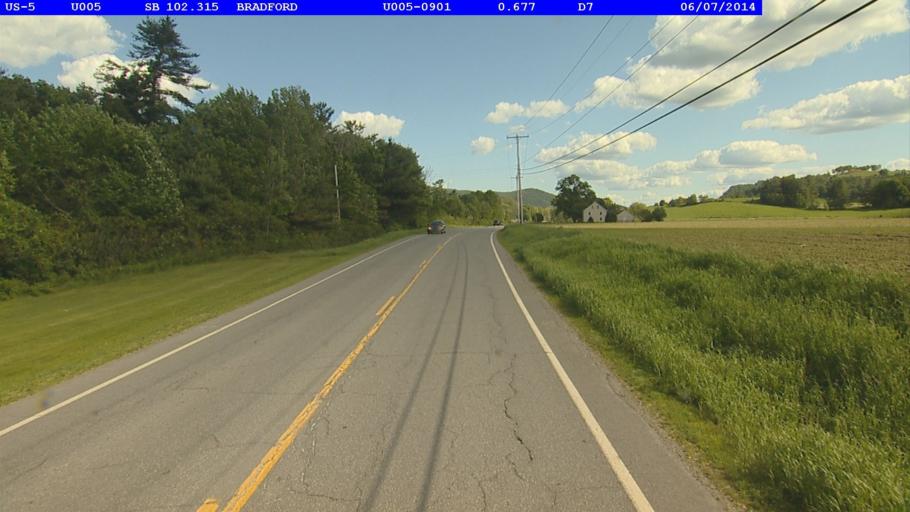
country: US
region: New Hampshire
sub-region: Grafton County
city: Orford
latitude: 43.9713
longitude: -72.1161
